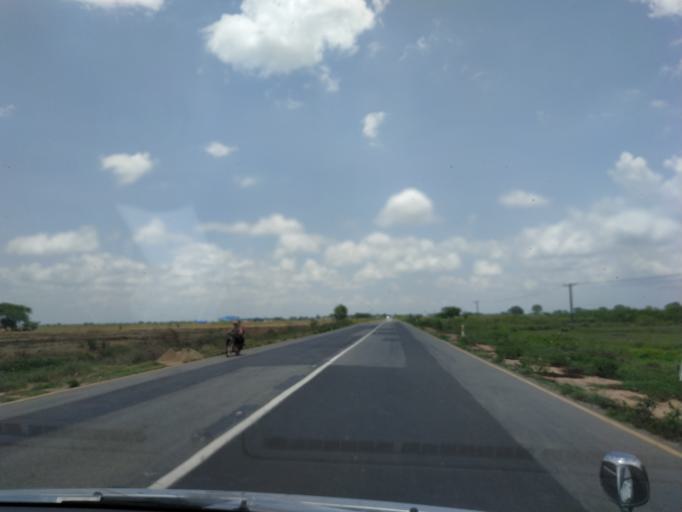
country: MM
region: Bago
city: Thanatpin
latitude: 17.4599
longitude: 96.5992
